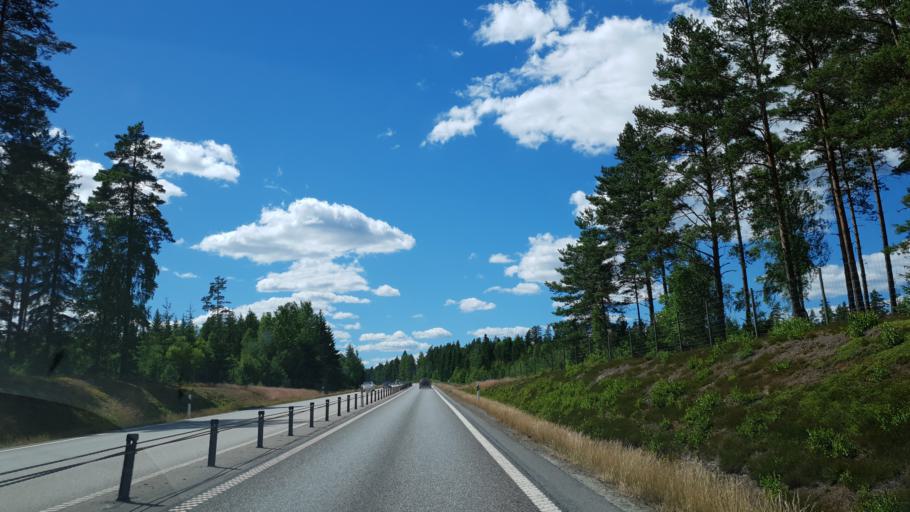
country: SE
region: Kronoberg
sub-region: Vaxjo Kommun
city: Ingelstad
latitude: 56.8699
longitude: 14.9929
